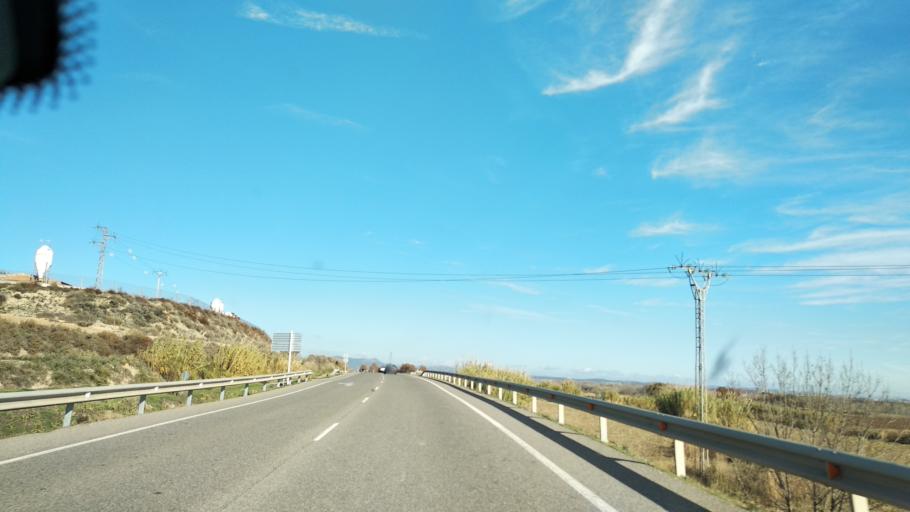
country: ES
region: Catalonia
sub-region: Provincia de Lleida
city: Termens
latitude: 41.7396
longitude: 0.7544
